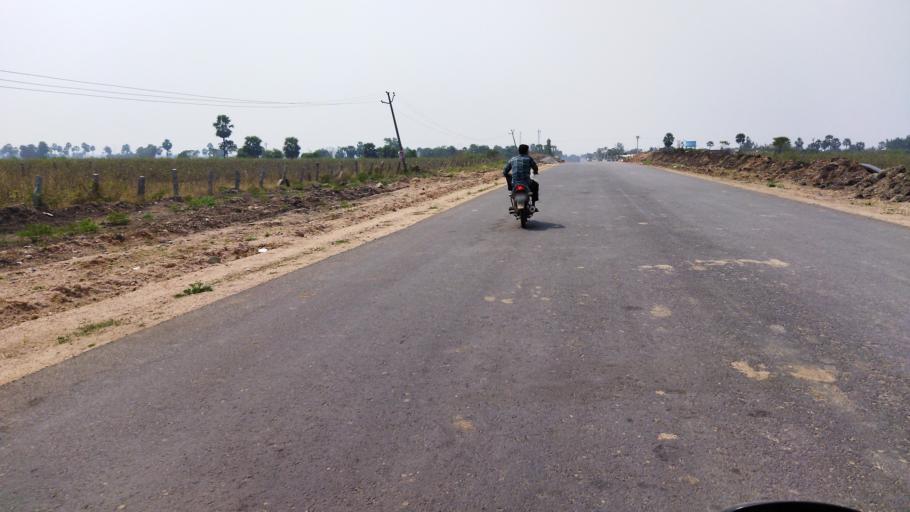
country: IN
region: Telangana
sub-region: Nalgonda
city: Nalgonda
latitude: 17.1484
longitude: 79.4006
